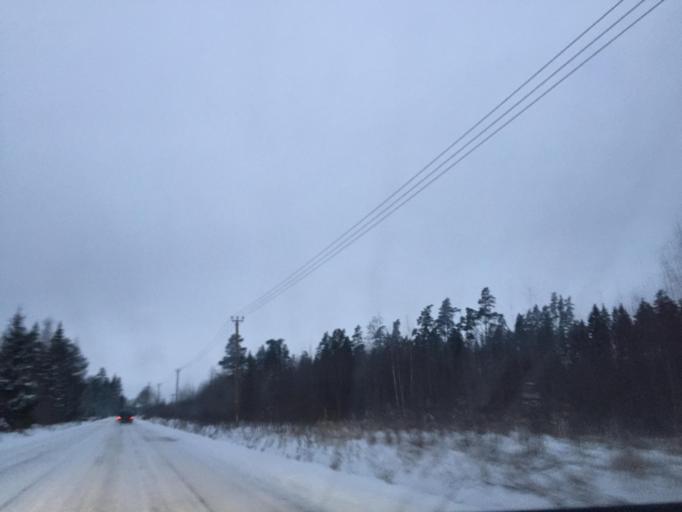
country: LV
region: Raunas
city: Rauna
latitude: 57.4282
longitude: 25.6690
